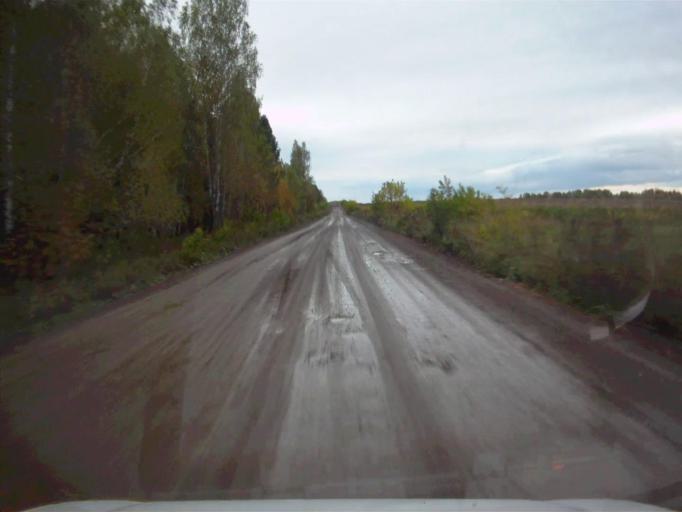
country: RU
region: Sverdlovsk
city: Mikhaylovsk
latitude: 56.1591
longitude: 59.2519
